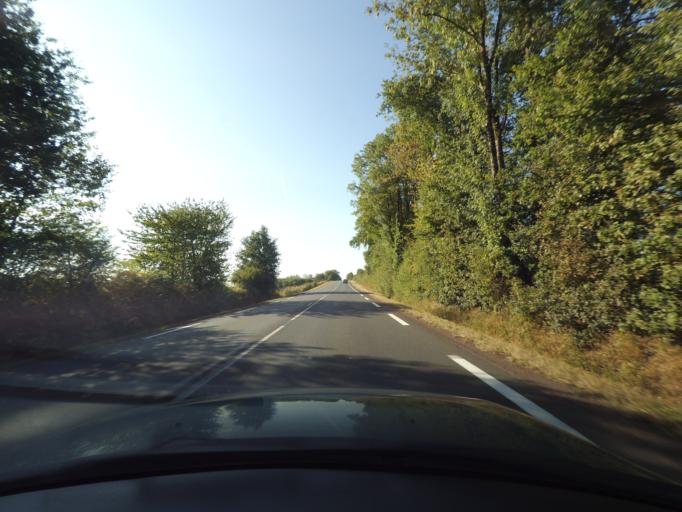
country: FR
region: Poitou-Charentes
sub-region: Departement des Deux-Sevres
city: Viennay
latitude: 46.6916
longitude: -0.2733
